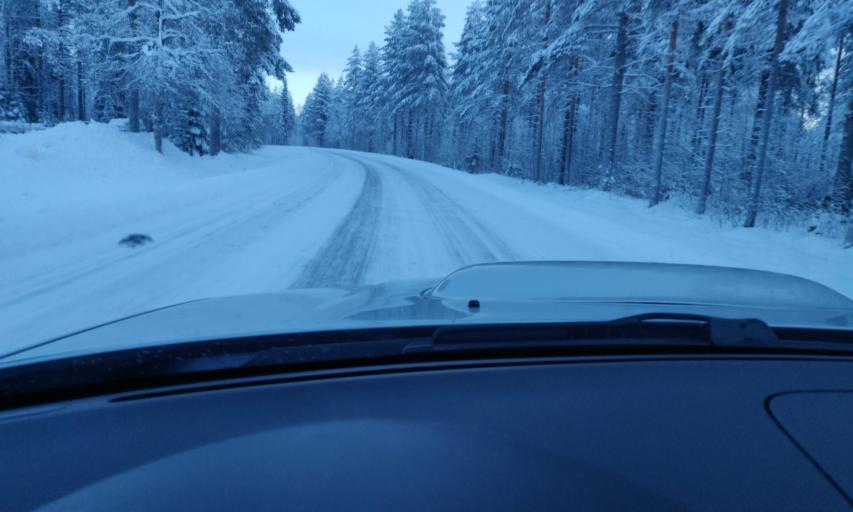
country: FI
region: Kainuu
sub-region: Kehys-Kainuu
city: Suomussalmi
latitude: 64.9006
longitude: 29.0295
